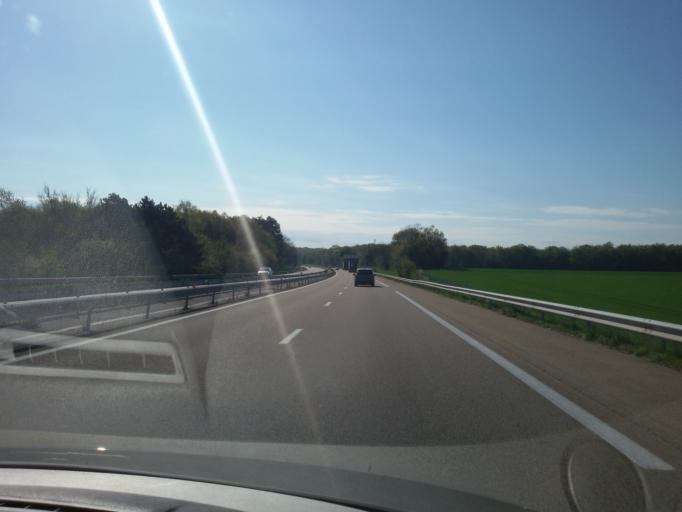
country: FR
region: Bourgogne
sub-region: Departement de l'Yonne
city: Vermenton
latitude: 47.7203
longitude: 3.7577
